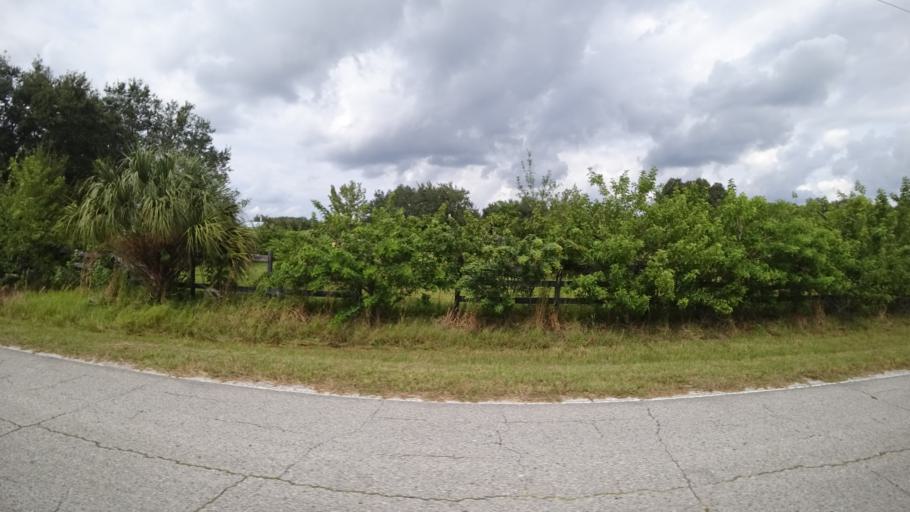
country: US
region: Florida
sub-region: Manatee County
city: Ellenton
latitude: 27.4878
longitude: -82.3773
